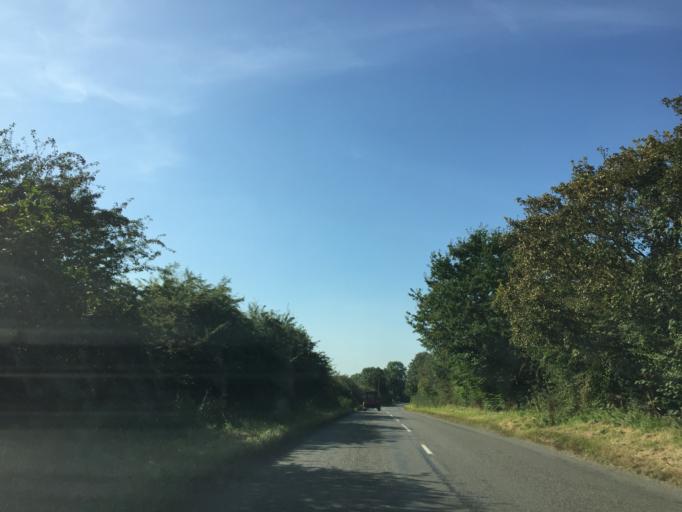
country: GB
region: England
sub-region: Leicestershire
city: Queniborough
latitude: 52.7010
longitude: -1.0275
